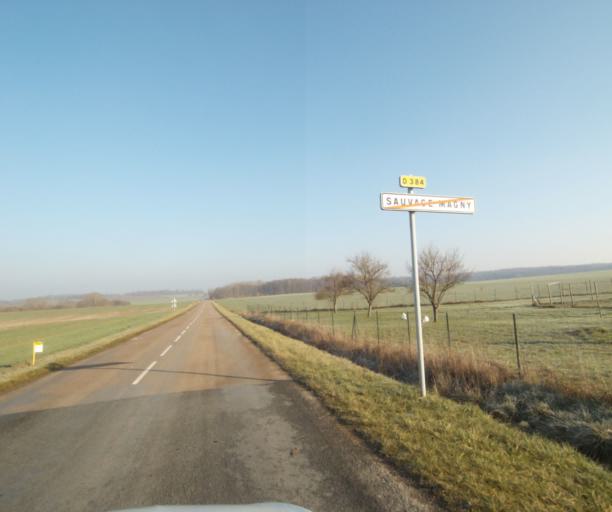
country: FR
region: Champagne-Ardenne
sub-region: Departement de la Haute-Marne
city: Montier-en-Der
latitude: 48.4155
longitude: 4.7418
